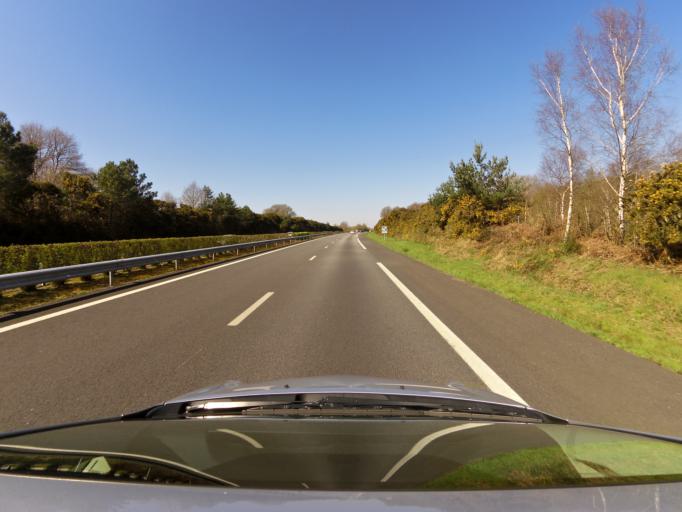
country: FR
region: Brittany
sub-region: Departement du Morbihan
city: Beignon
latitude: 47.9244
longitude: -2.1694
